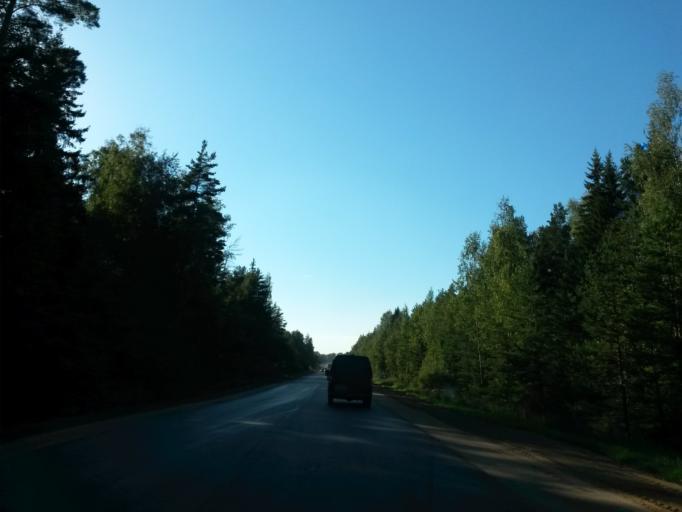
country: RU
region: Ivanovo
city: Novo-Talitsy
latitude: 57.0195
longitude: 40.7769
